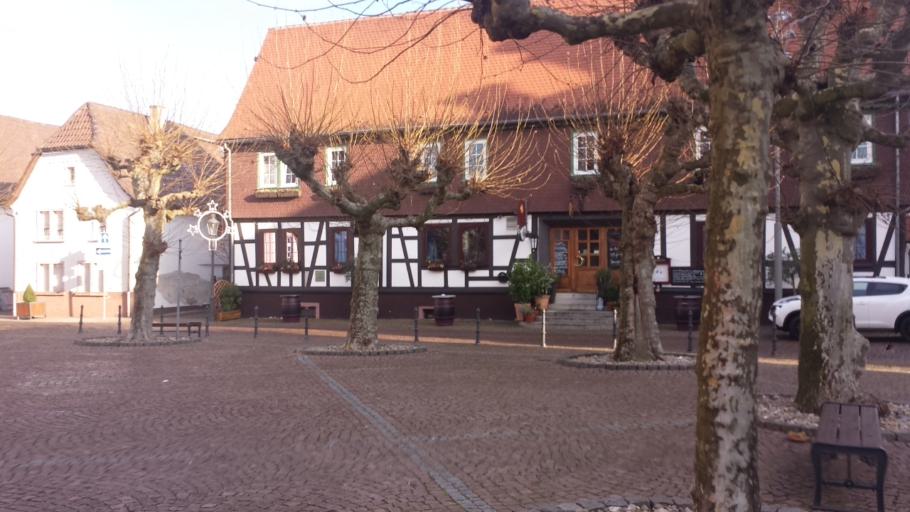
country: DE
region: Hesse
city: Heusenstamm
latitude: 50.0597
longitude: 8.8065
